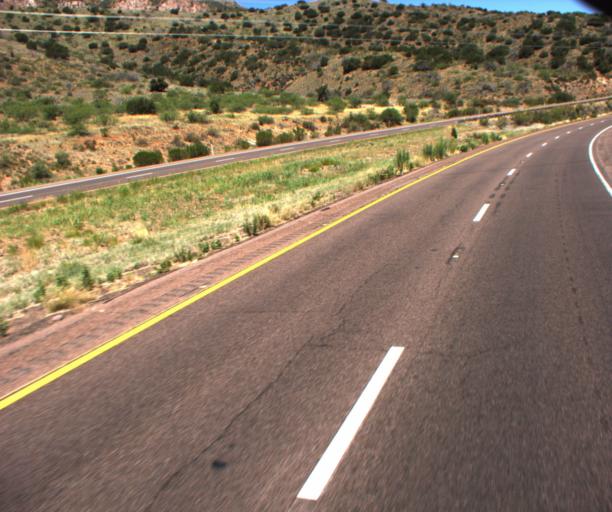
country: US
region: Arizona
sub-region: Gila County
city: Tonto Basin
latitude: 34.0114
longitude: -111.3593
